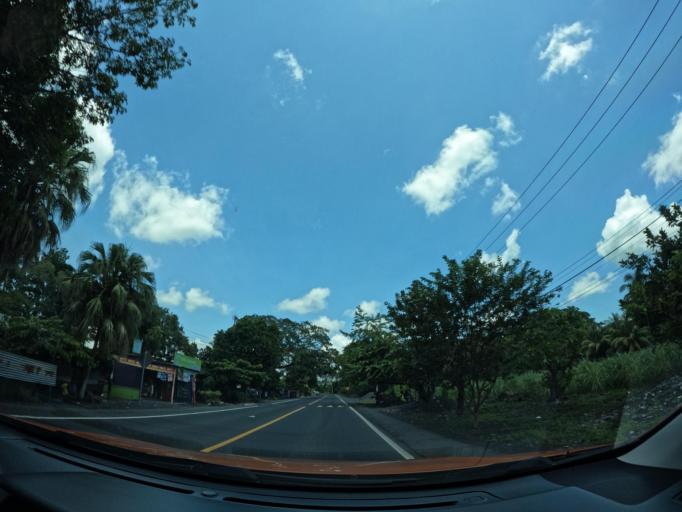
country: GT
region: Escuintla
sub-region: Municipio de Masagua
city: Masagua
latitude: 14.1536
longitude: -90.8830
